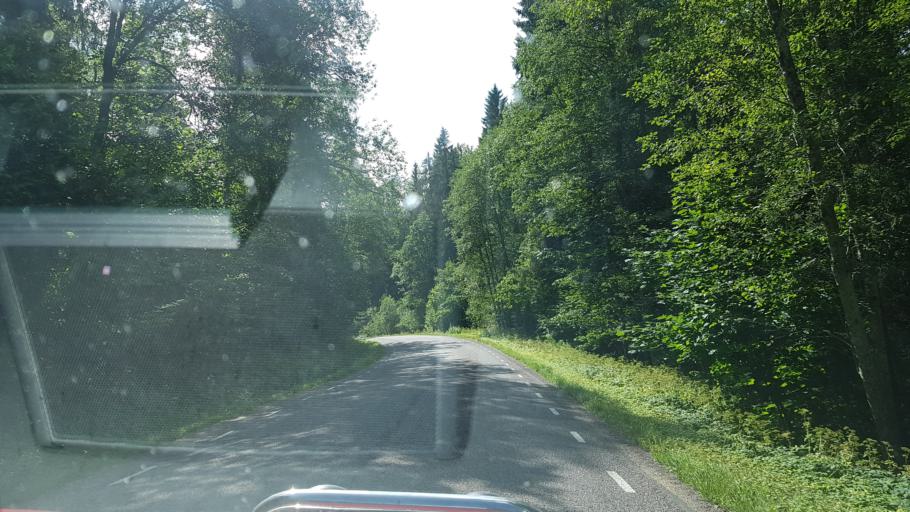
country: EE
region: Vorumaa
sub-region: Voru linn
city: Voru
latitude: 57.6564
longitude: 27.0862
